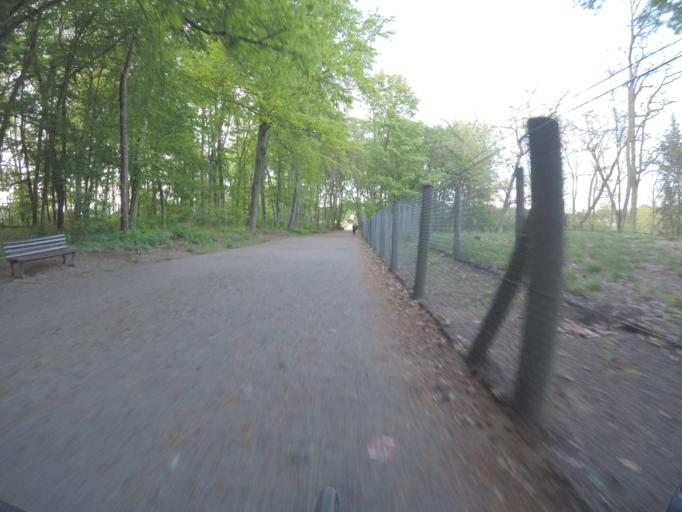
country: DE
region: Berlin
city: Reinickendorf
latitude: 52.5521
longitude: 13.3247
